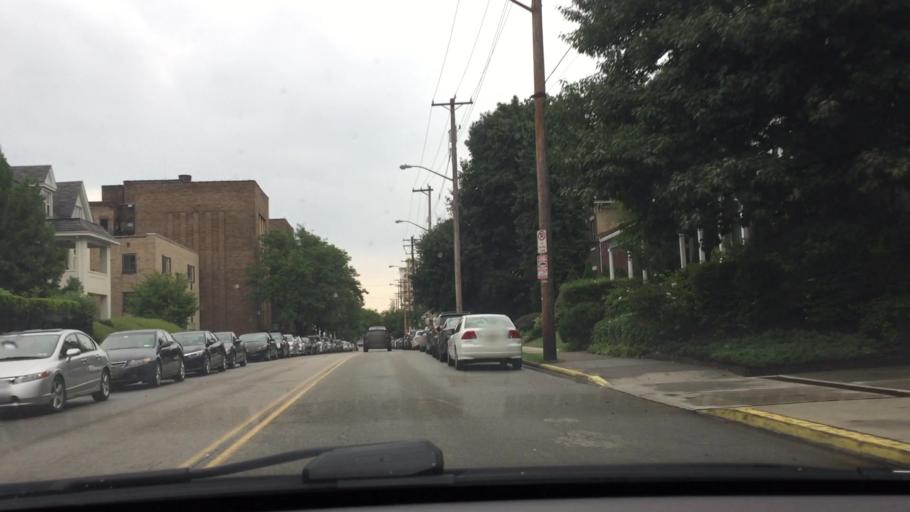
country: US
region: Pennsylvania
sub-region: Allegheny County
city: Bloomfield
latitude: 40.4552
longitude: -79.9253
